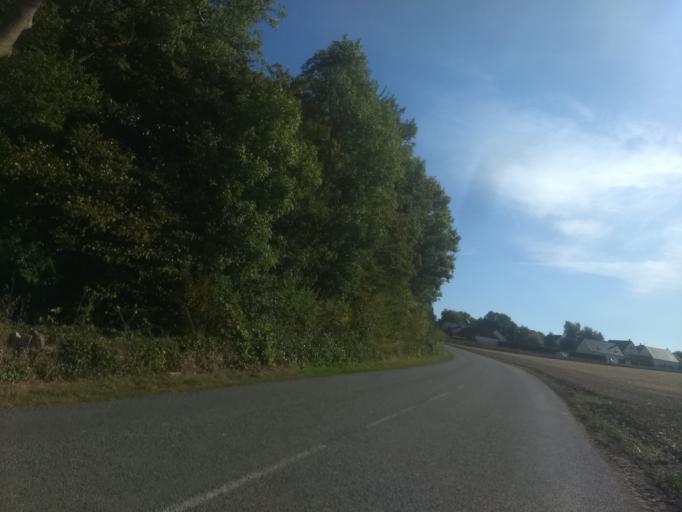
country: FR
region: Nord-Pas-de-Calais
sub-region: Departement du Pas-de-Calais
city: Roeux
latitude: 50.2752
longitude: 2.8930
